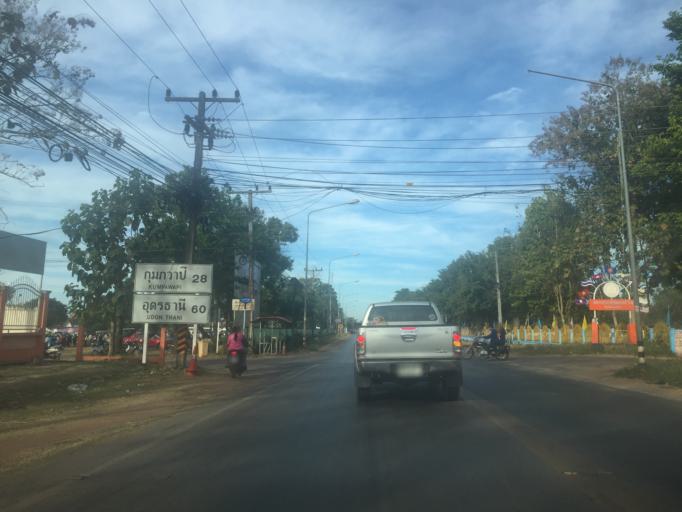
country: TH
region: Changwat Udon Thani
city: Si That
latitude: 16.9744
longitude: 103.2187
